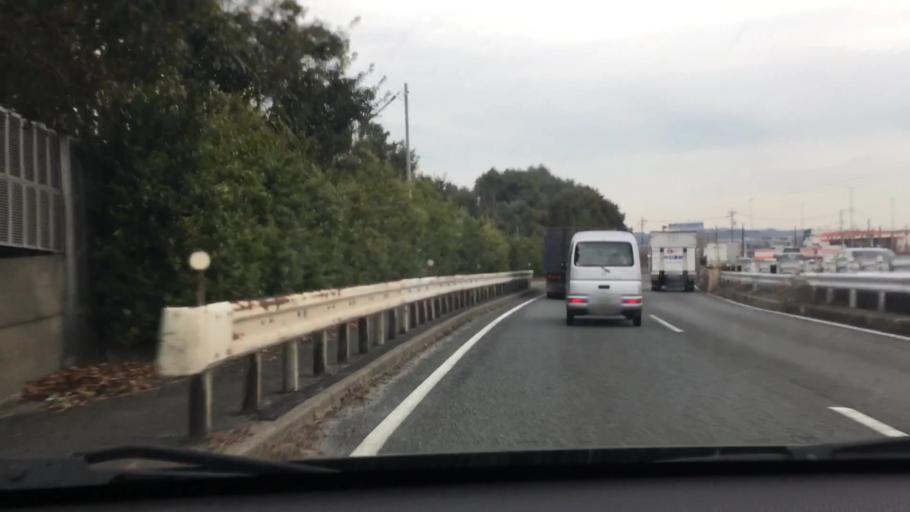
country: JP
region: Mie
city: Suzuka
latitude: 34.8899
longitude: 136.5335
